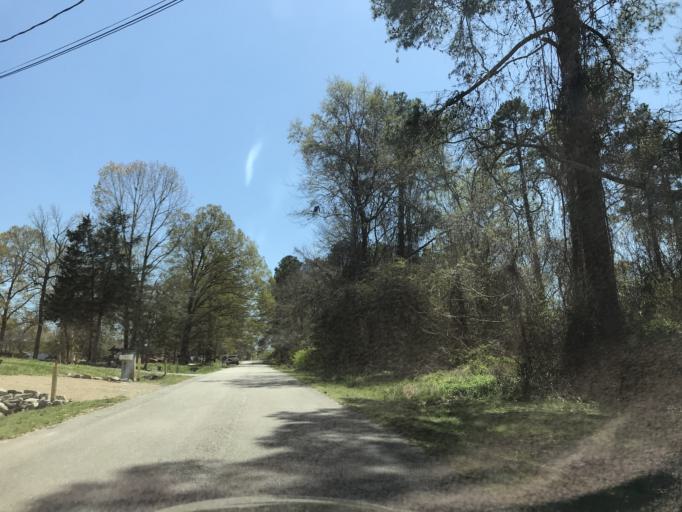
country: US
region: North Carolina
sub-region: Wake County
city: Raleigh
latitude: 35.8139
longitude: -78.5744
